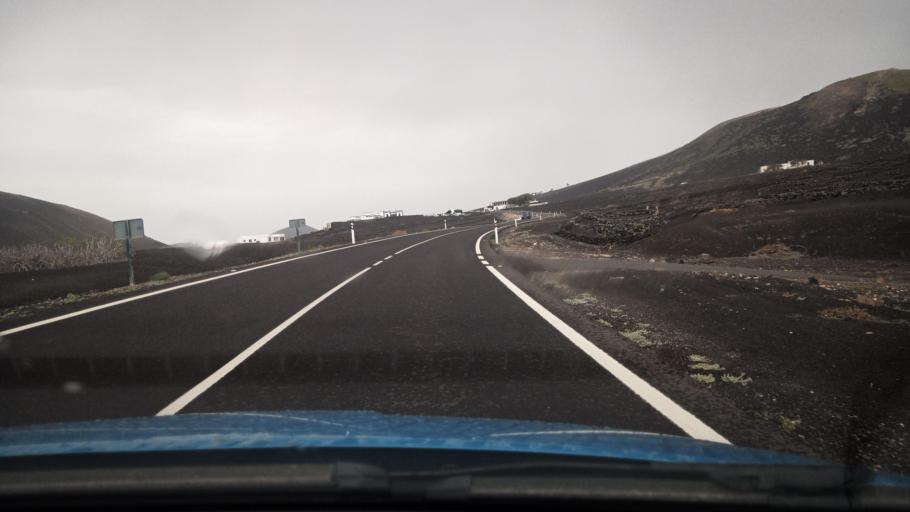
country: ES
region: Canary Islands
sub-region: Provincia de Las Palmas
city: Yaiza
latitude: 28.9667
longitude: -13.7200
